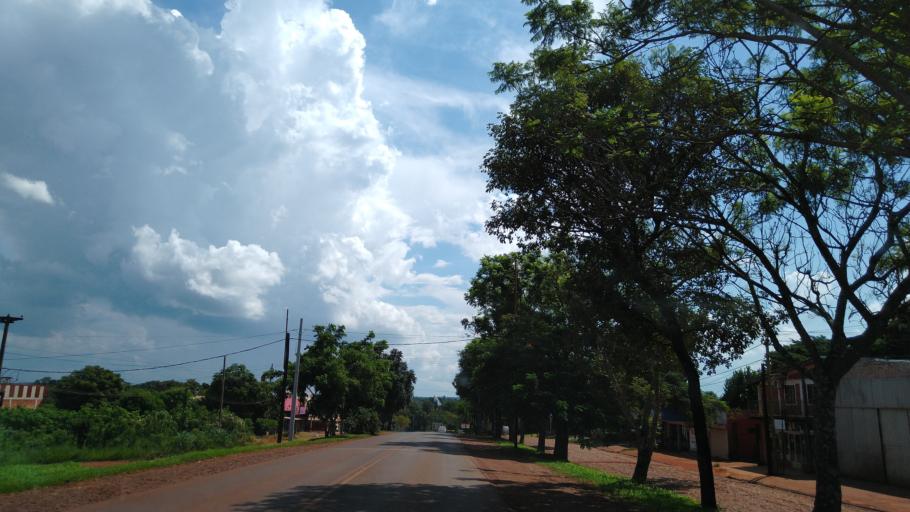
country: AR
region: Misiones
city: Puerto Libertad
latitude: -25.9701
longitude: -54.5761
